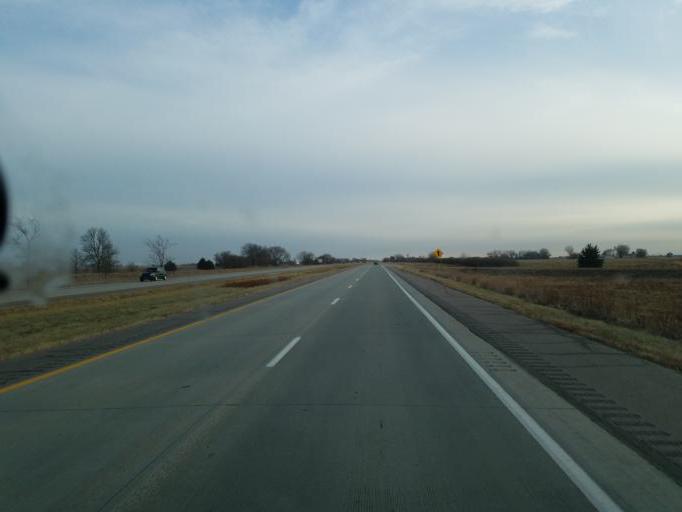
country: US
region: Iowa
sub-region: Monona County
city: Onawa
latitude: 42.1271
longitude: -96.2040
